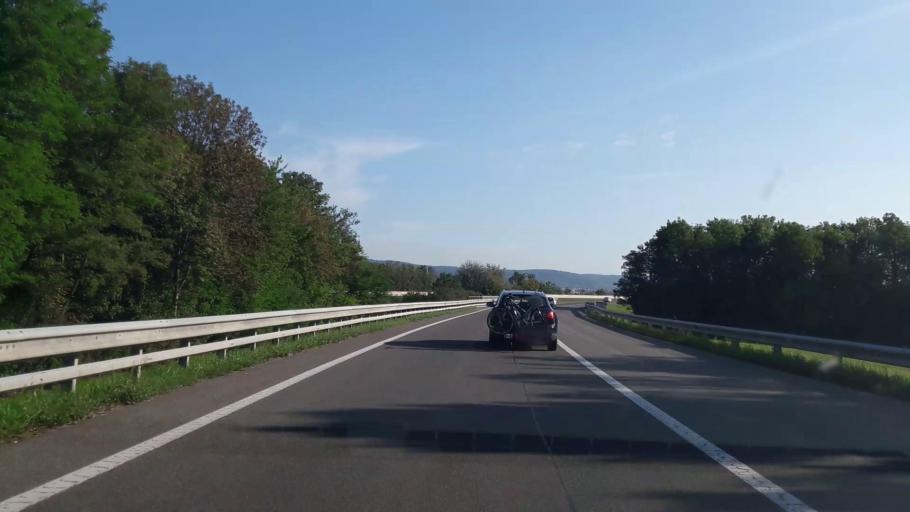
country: AT
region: Burgenland
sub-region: Eisenstadt-Umgebung
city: Wulkaprodersdorf
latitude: 47.8151
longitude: 16.4983
